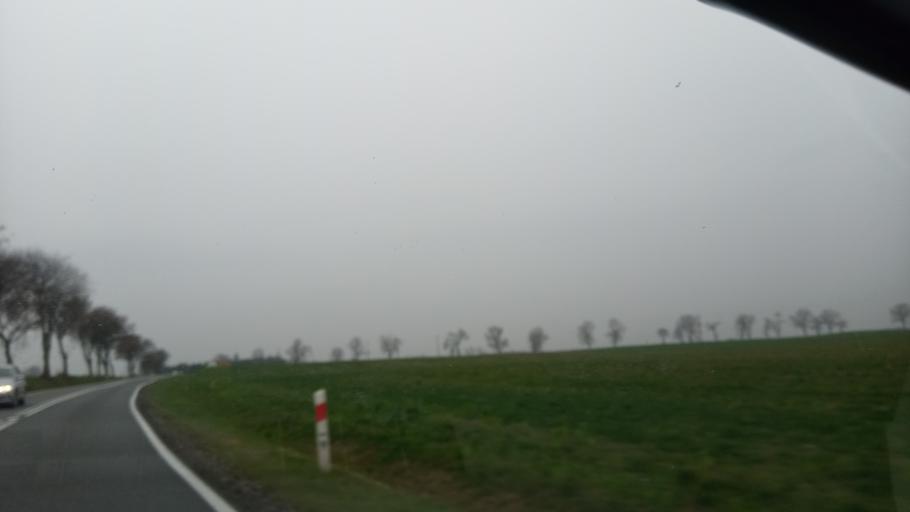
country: PL
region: Kujawsko-Pomorskie
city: Kamien Krajenski
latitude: 53.5084
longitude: 17.5097
